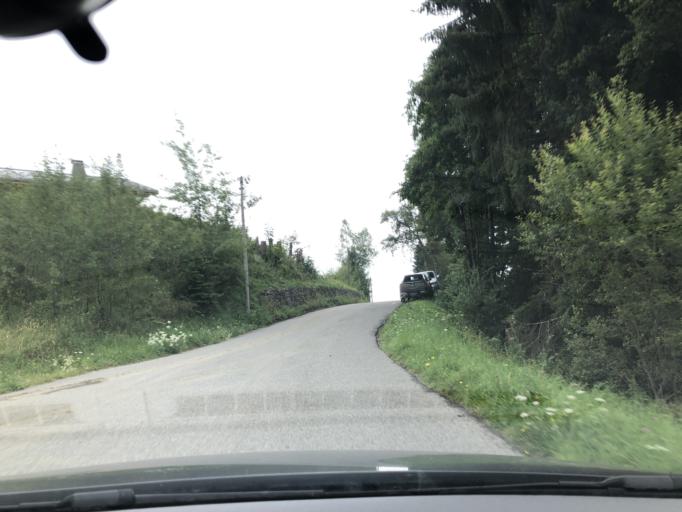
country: FR
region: Rhone-Alpes
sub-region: Departement de la Haute-Savoie
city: Combloux
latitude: 45.8943
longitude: 6.6197
